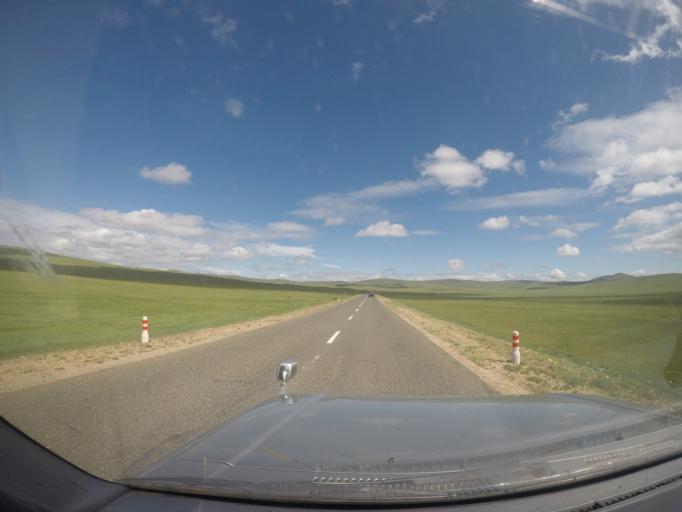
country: MN
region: Hentiy
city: Modot
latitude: 47.6027
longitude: 109.2250
